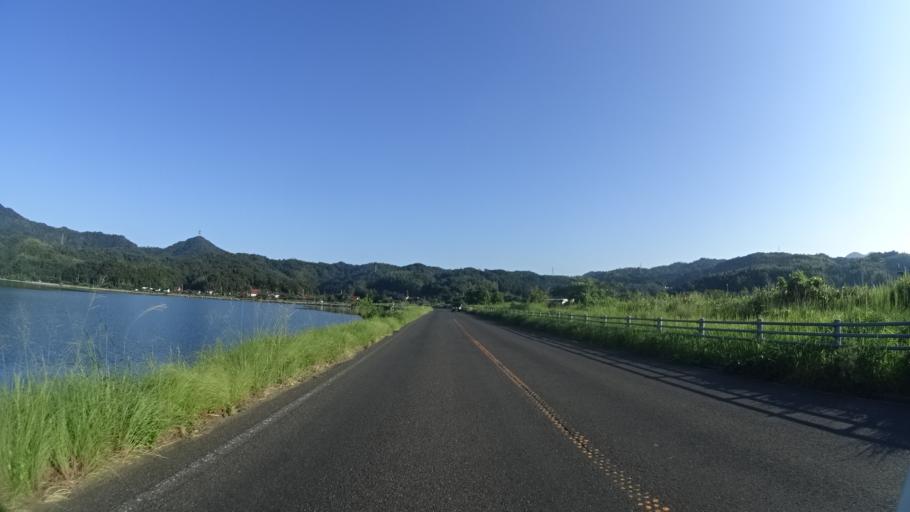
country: JP
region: Shimane
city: Sakaiminato
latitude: 35.5340
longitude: 133.1610
